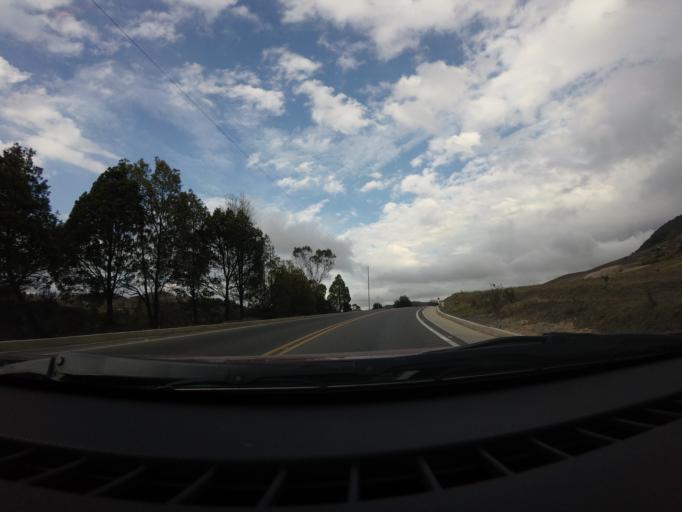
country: CO
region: Boyaca
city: Cucaita
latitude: 5.5647
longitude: -73.4290
